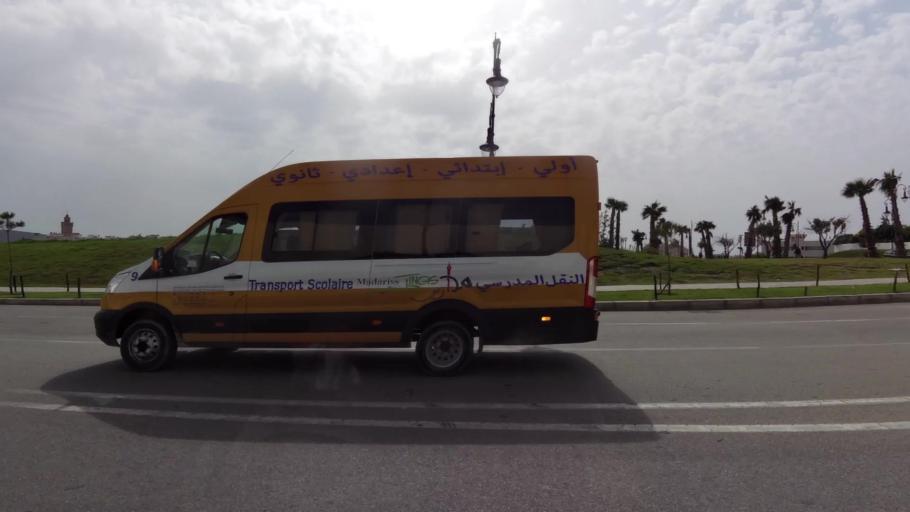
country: MA
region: Tanger-Tetouan
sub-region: Tanger-Assilah
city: Boukhalef
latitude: 35.7382
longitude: -5.8751
